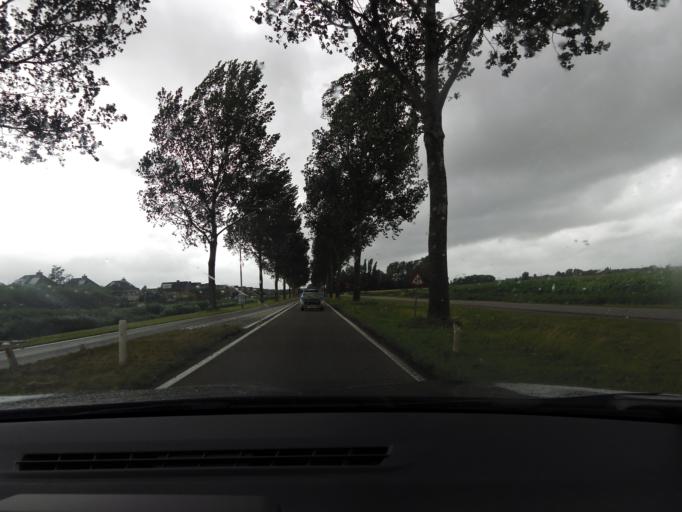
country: NL
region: South Holland
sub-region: Gemeente Hellevoetsluis
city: Nieuwenhoorn
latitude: 51.8483
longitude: 4.1656
